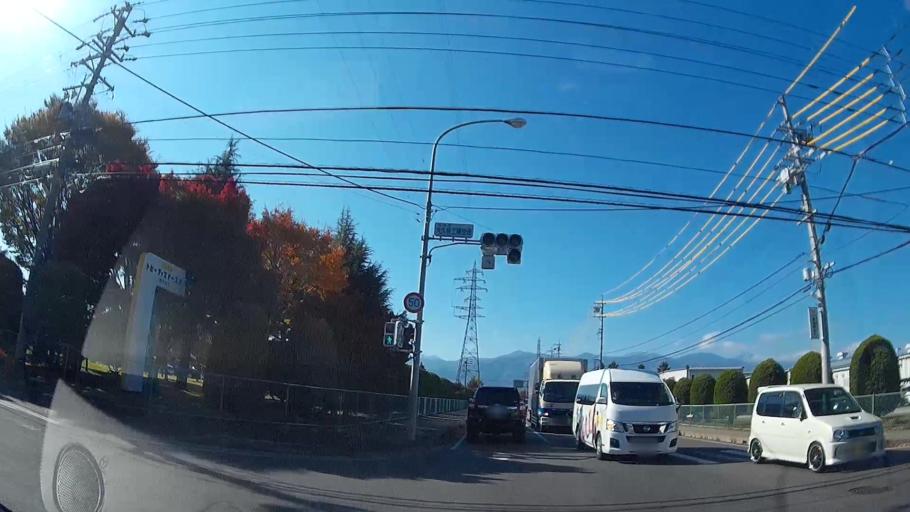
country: JP
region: Nagano
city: Matsumoto
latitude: 36.2050
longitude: 137.9349
